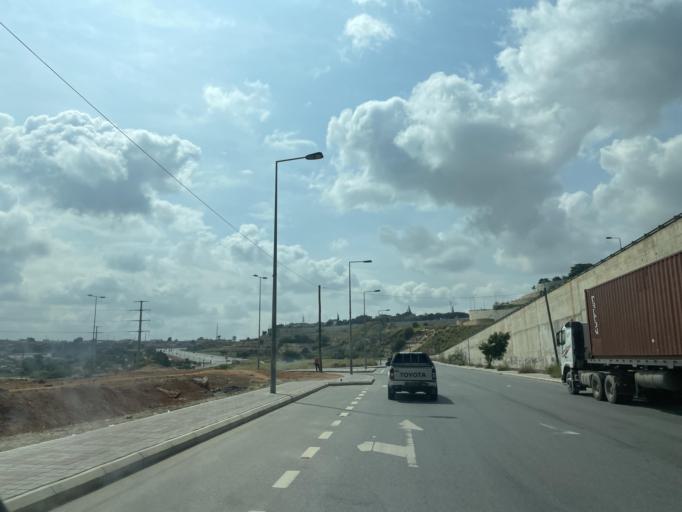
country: AO
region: Luanda
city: Luanda
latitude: -8.8051
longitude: 13.2514
